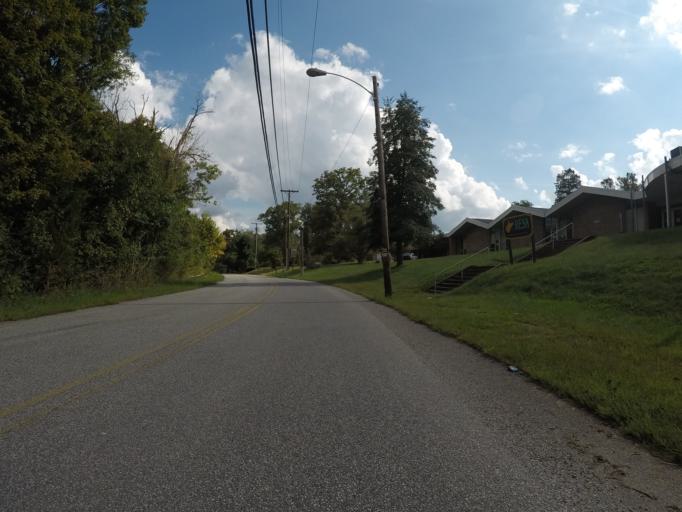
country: US
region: West Virginia
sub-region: Cabell County
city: Huntington
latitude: 38.3968
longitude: -82.4343
